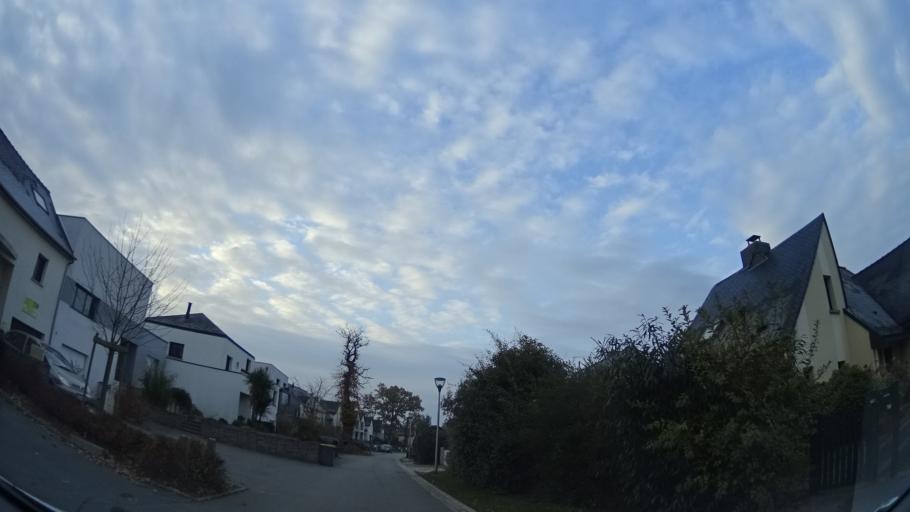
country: FR
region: Brittany
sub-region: Departement d'Ille-et-Vilaine
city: La Chapelle-des-Fougeretz
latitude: 48.1855
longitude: -1.7283
